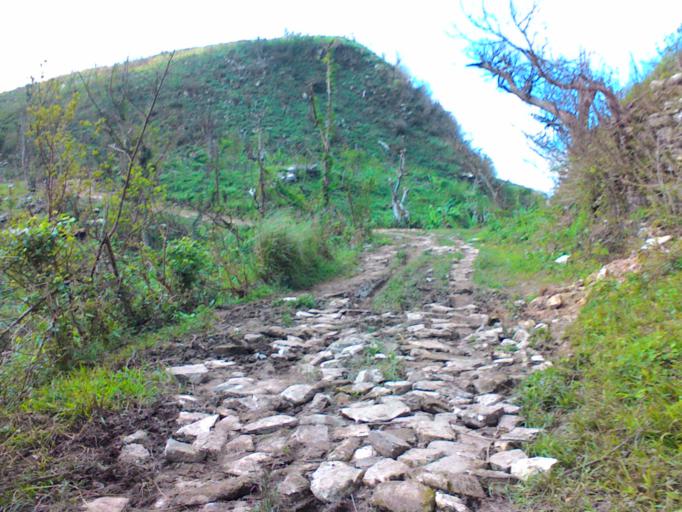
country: HT
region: Grandans
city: Moron
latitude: 18.4606
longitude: -74.1160
